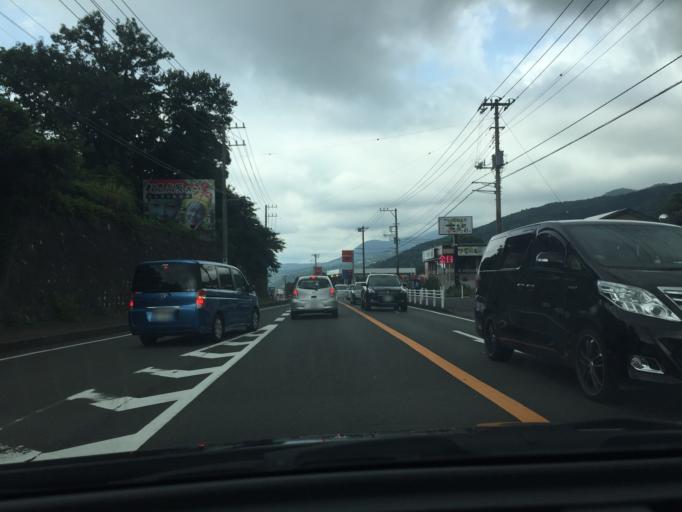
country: JP
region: Shizuoka
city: Ito
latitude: 34.8802
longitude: 139.1065
